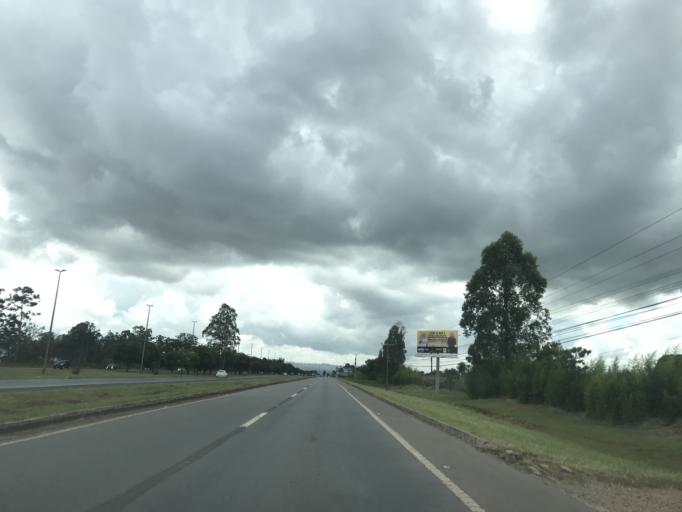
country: BR
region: Federal District
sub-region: Brasilia
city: Brasilia
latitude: -15.6870
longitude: -47.8530
